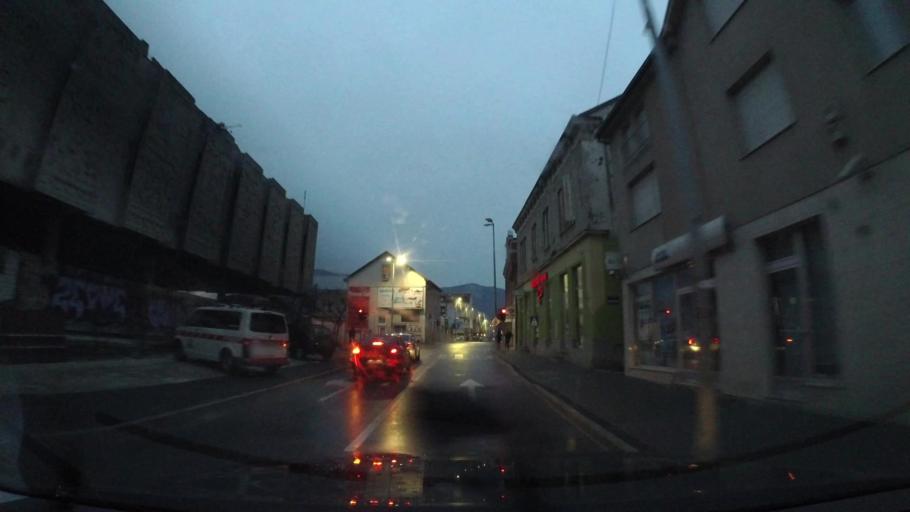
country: BA
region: Federation of Bosnia and Herzegovina
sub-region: Hercegovacko-Bosanski Kanton
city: Mostar
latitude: 43.3440
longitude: 17.8138
